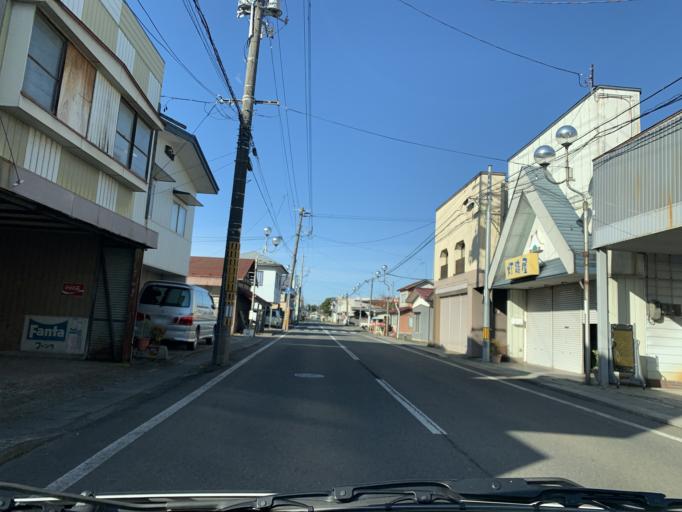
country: JP
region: Iwate
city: Mizusawa
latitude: 39.1978
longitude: 141.1180
